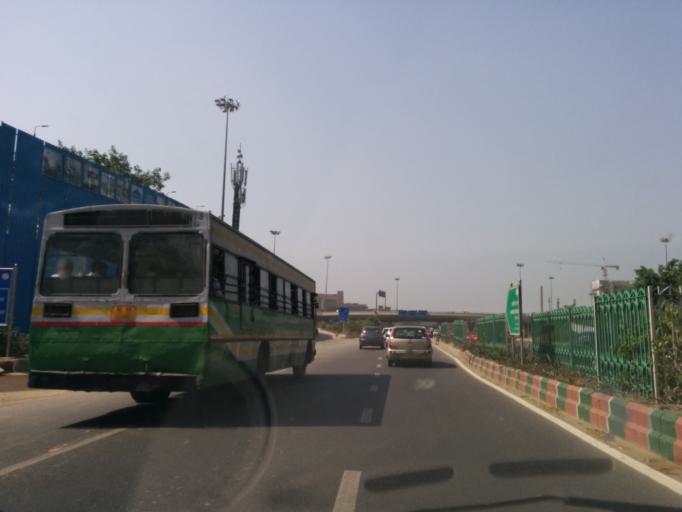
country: IN
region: NCT
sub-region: New Delhi
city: New Delhi
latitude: 28.5726
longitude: 77.2093
